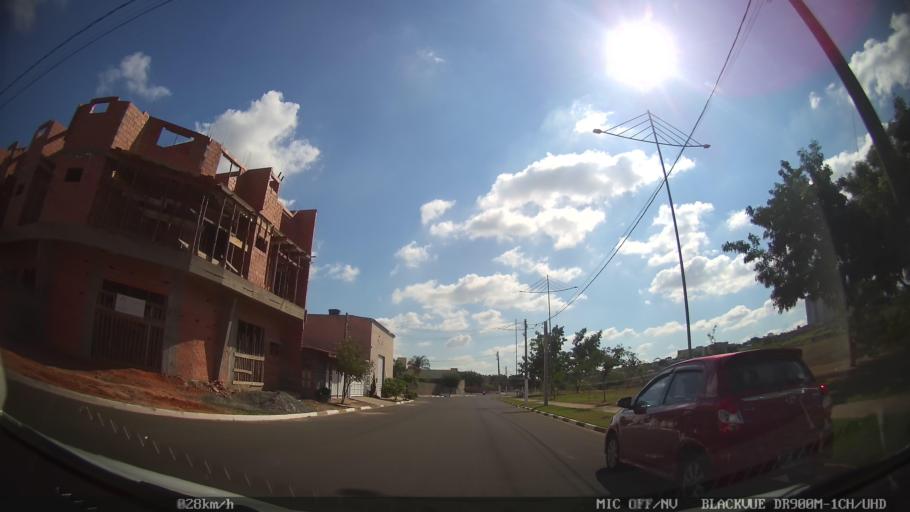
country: BR
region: Sao Paulo
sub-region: Hortolandia
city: Hortolandia
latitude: -22.8816
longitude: -47.2151
